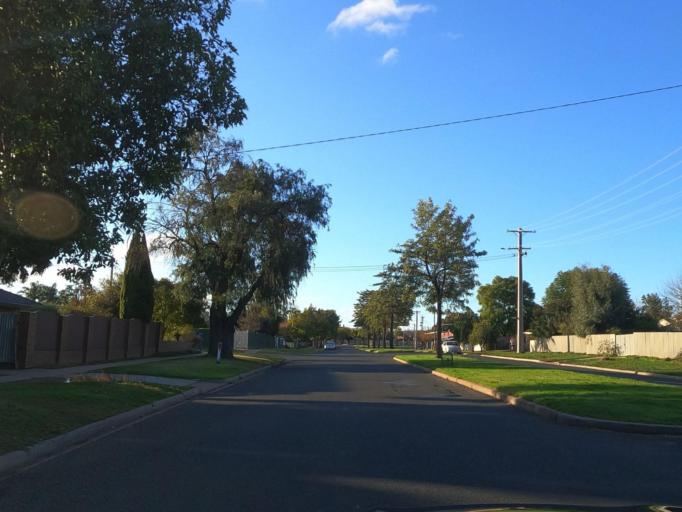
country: AU
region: Victoria
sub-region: Swan Hill
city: Swan Hill
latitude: -35.3458
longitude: 143.5558
